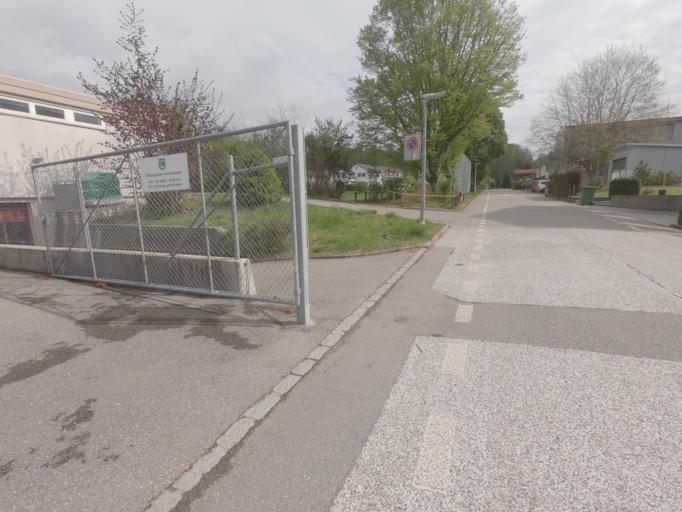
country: CH
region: Solothurn
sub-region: Bezirk Lebern
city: Riedholz
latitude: 47.2209
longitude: 7.5550
